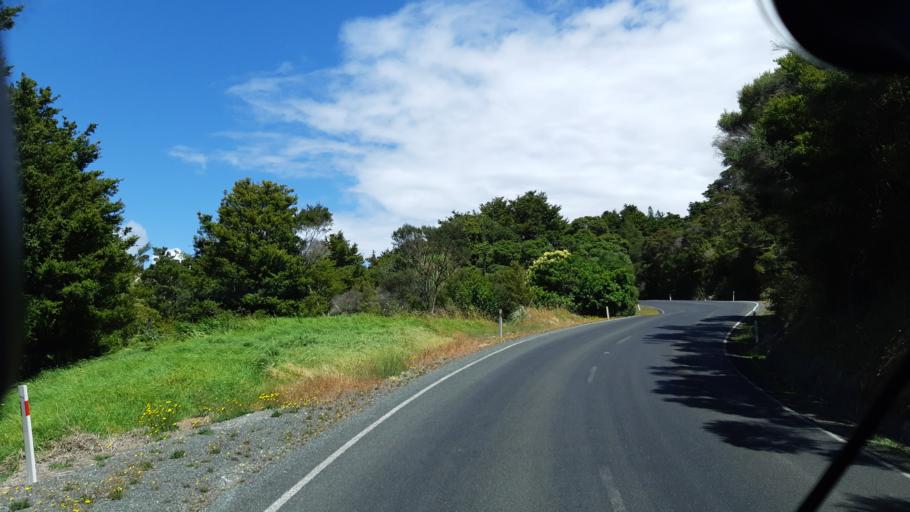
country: NZ
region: Northland
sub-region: Far North District
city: Kaitaia
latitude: -35.2714
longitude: 173.4832
